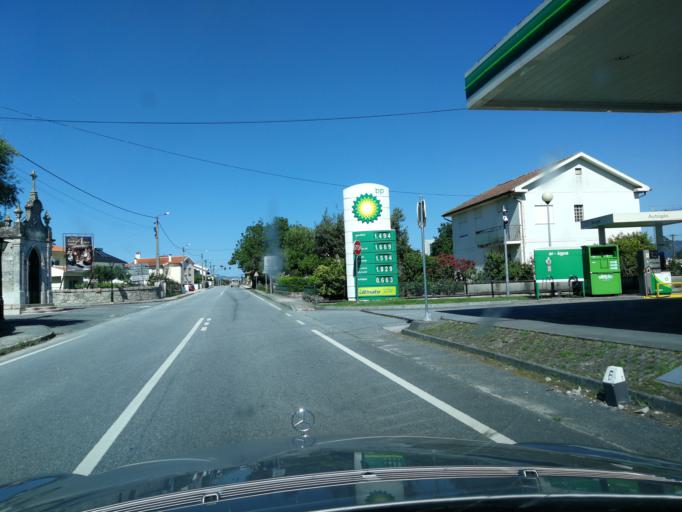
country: PT
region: Viana do Castelo
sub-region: Viana do Castelo
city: Darque
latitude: 41.7117
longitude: -8.7423
